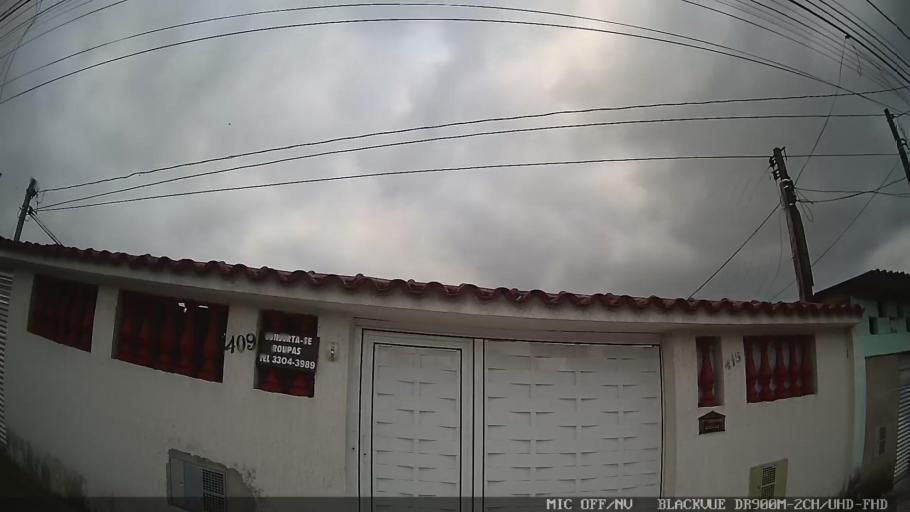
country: BR
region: Sao Paulo
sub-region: Santos
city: Santos
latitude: -23.9429
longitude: -46.2947
